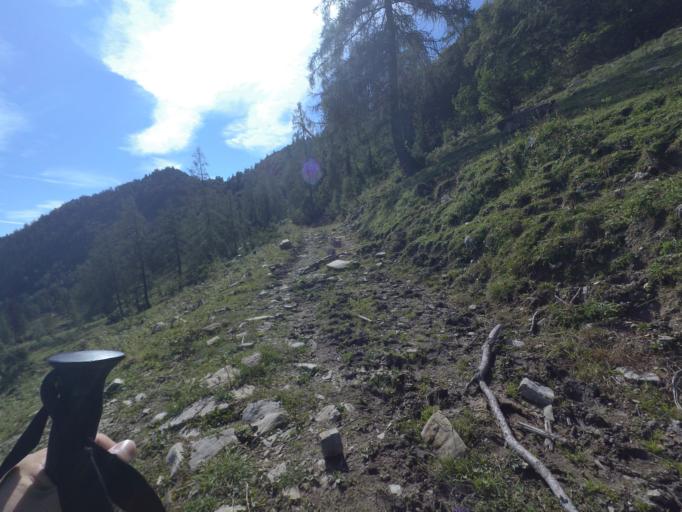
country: AT
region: Salzburg
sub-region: Politischer Bezirk Salzburg-Umgebung
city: Hintersee
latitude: 47.6944
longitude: 13.2584
